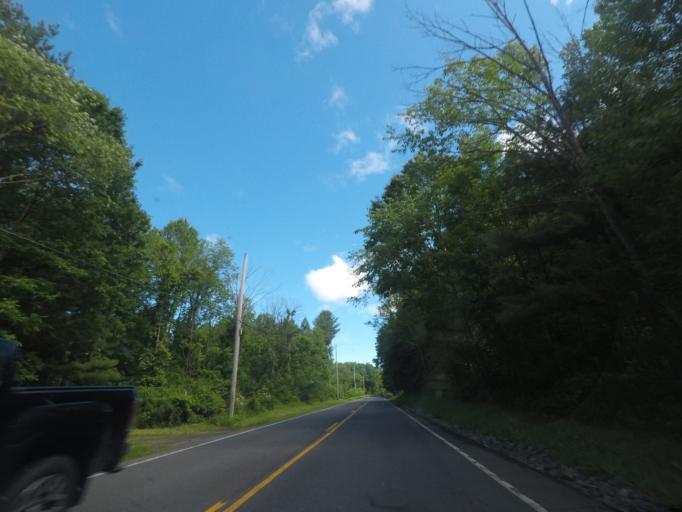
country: US
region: New York
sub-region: Columbia County
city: Philmont
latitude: 42.2018
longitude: -73.6289
